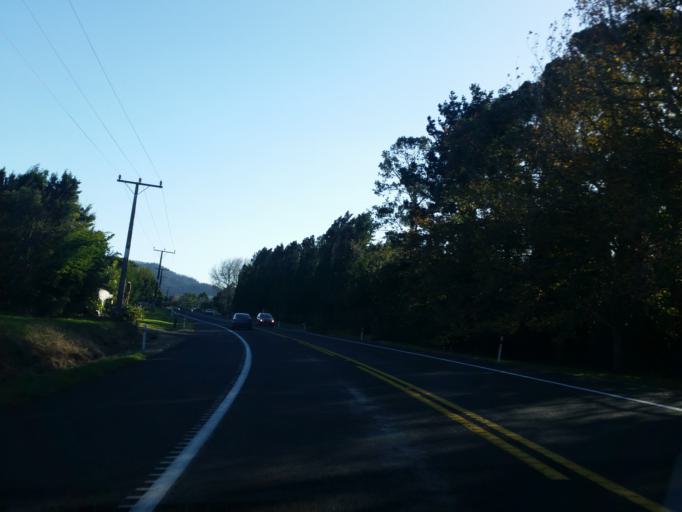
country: NZ
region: Bay of Plenty
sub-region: Western Bay of Plenty District
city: Katikati
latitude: -37.5221
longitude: 175.9201
